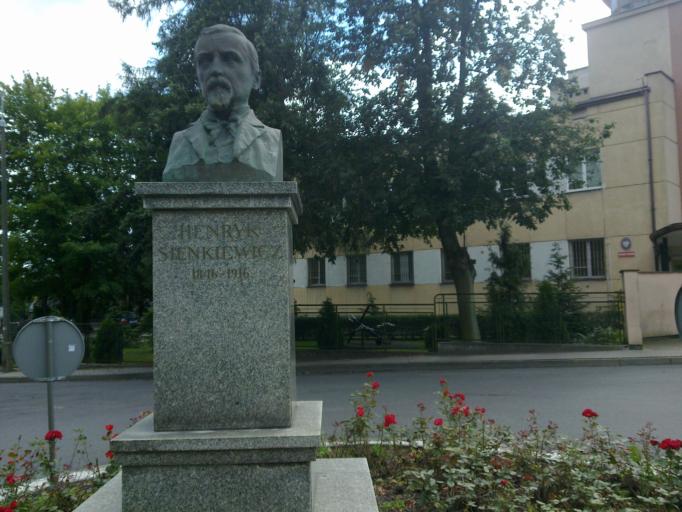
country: PL
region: Pomeranian Voivodeship
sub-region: Gdynia
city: Gdynia
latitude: 54.5112
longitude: 18.5493
